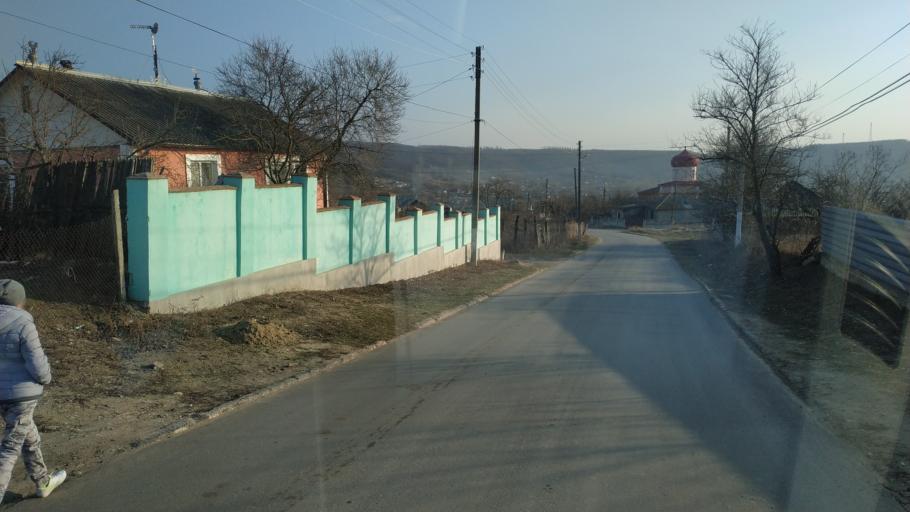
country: MD
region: Hincesti
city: Dancu
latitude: 46.7679
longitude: 28.3592
